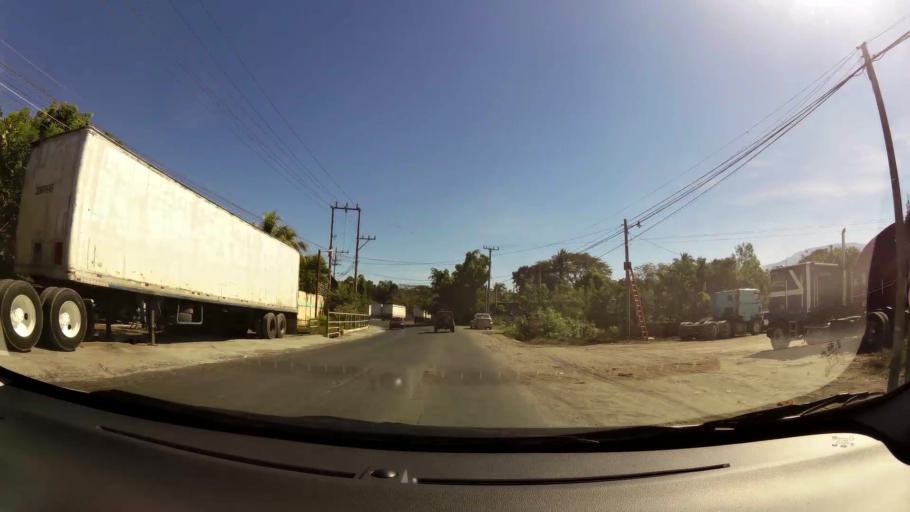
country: SV
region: La Libertad
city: San Juan Opico
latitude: 13.8001
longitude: -89.3619
